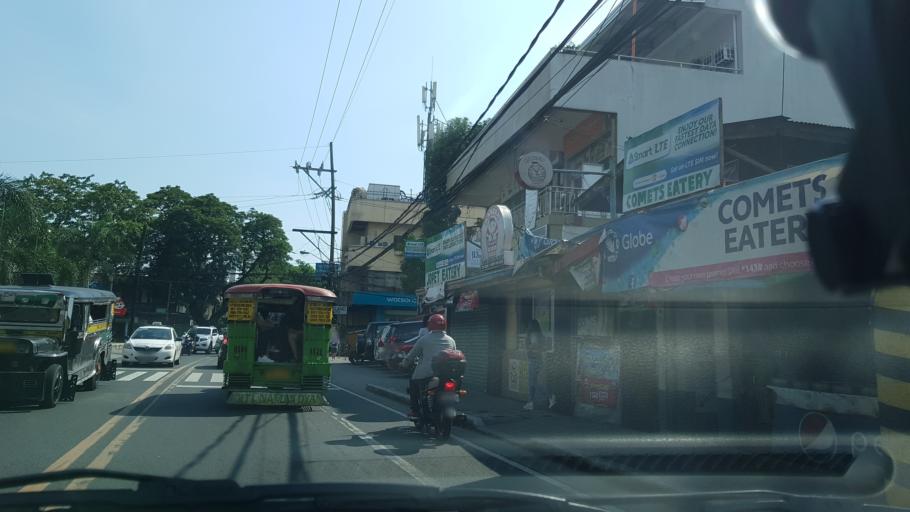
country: PH
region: Metro Manila
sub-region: Marikina
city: Calumpang
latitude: 14.6460
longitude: 121.0966
